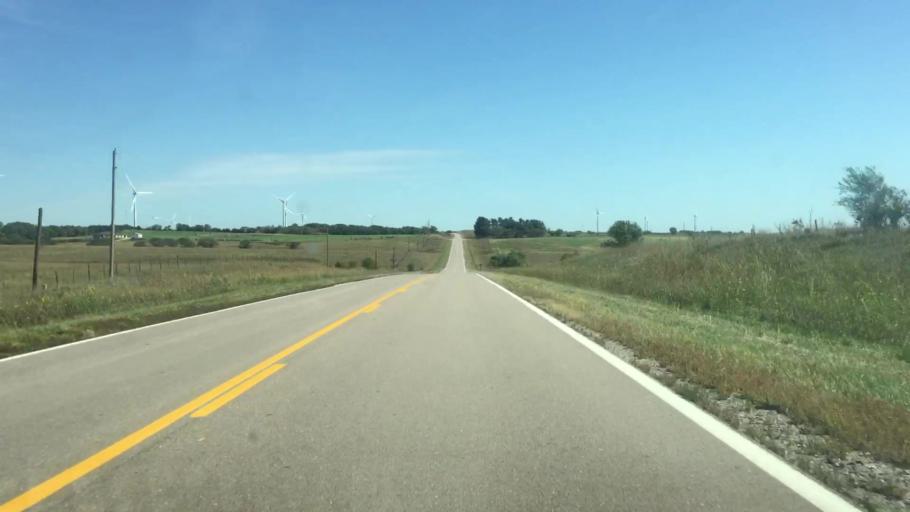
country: US
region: Nebraska
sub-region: Jefferson County
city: Fairbury
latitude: 40.0451
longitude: -96.9819
